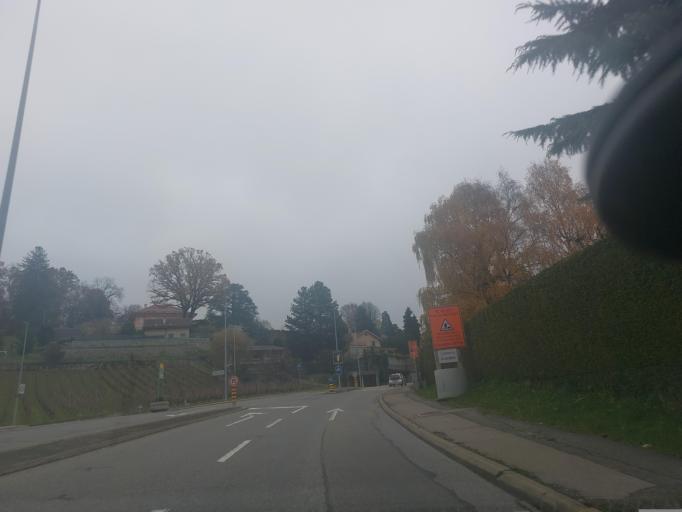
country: CH
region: Vaud
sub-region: Riviera-Pays-d'Enhaut District
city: La Tour-de-Peilz
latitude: 46.4721
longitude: 6.8693
